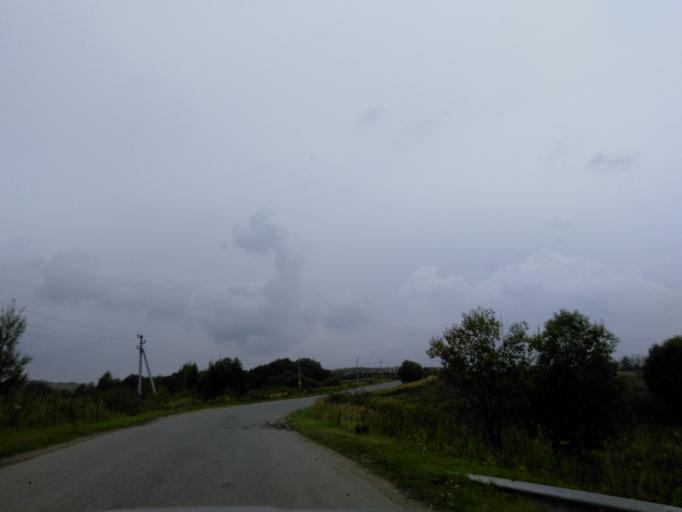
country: RU
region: Moskovskaya
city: Mendeleyevo
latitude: 56.1117
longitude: 37.2282
